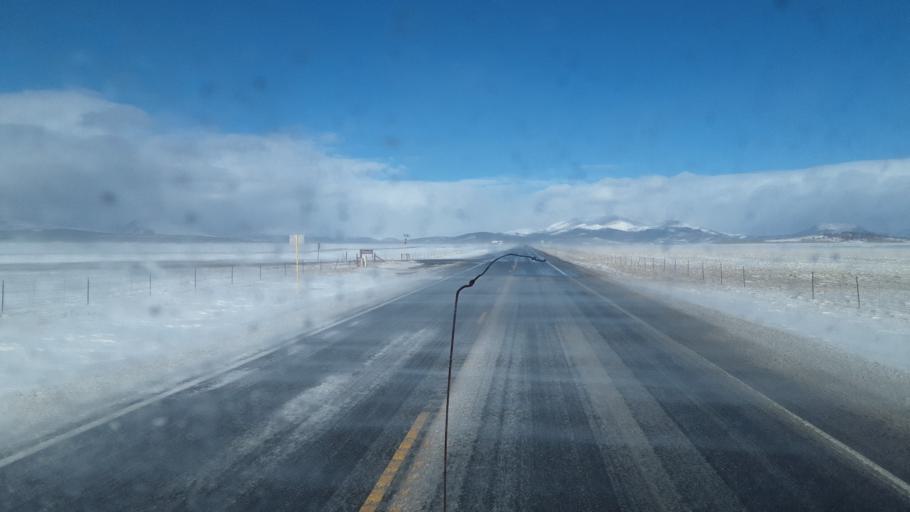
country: US
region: Colorado
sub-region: Park County
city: Fairplay
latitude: 39.1525
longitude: -105.9989
